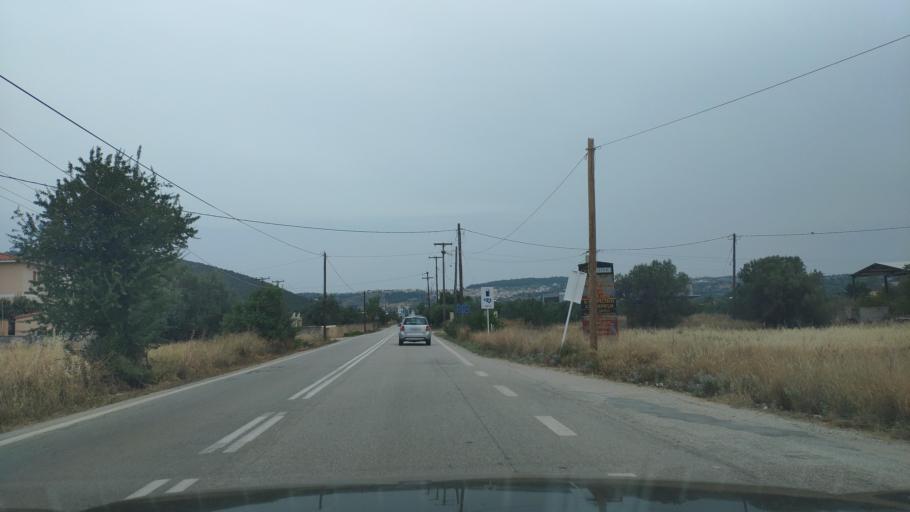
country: GR
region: Peloponnese
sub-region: Nomos Argolidos
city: Kranidi
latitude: 37.4073
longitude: 23.1542
